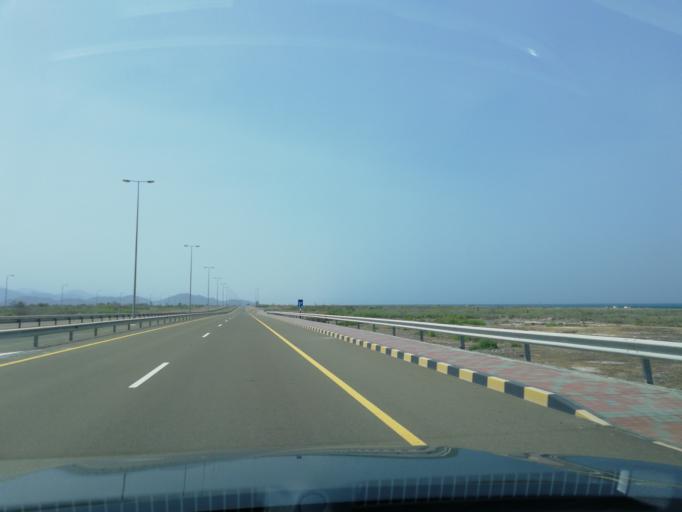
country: OM
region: Al Batinah
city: Shinas
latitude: 24.8980
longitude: 56.3979
